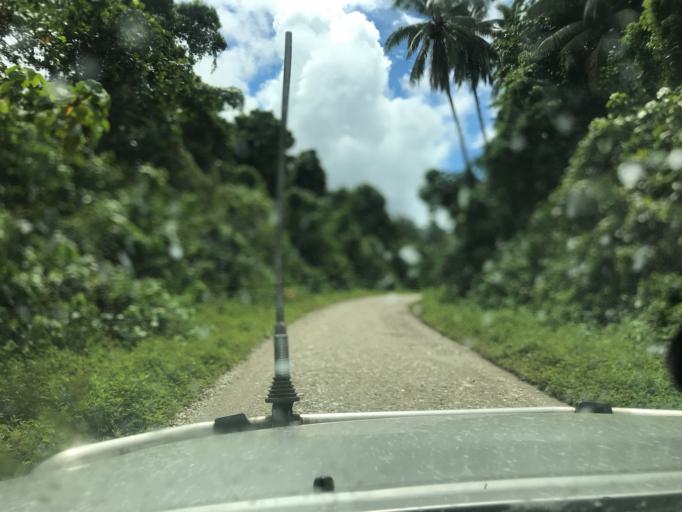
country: SB
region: Malaita
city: Auki
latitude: -8.3825
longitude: 160.7200
